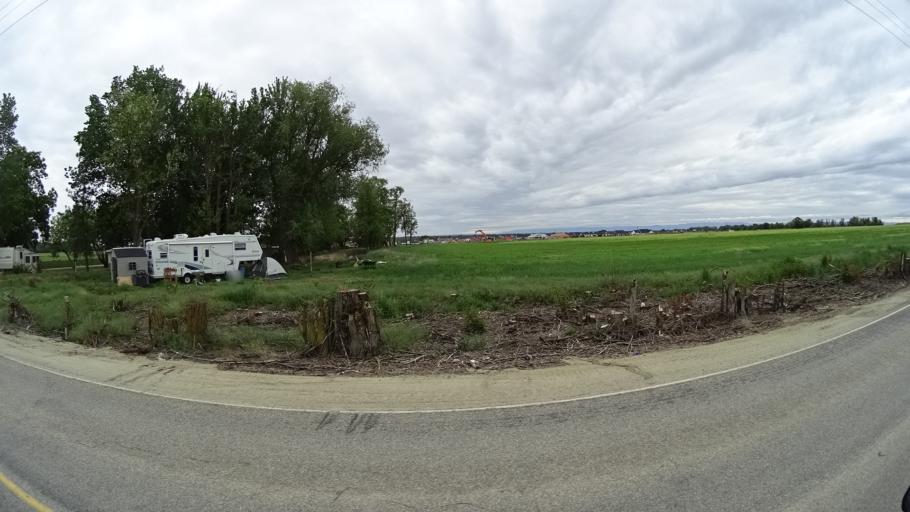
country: US
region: Idaho
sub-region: Ada County
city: Eagle
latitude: 43.7212
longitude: -116.4242
